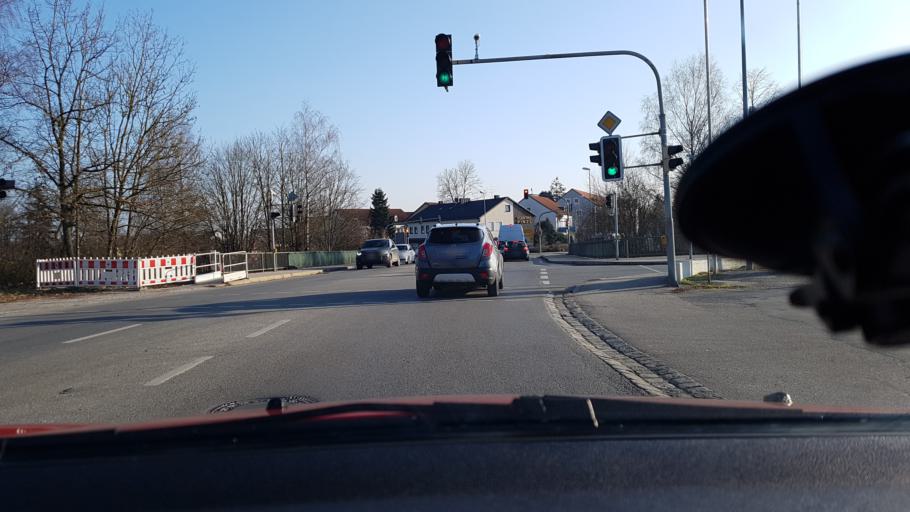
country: DE
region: Bavaria
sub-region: Lower Bavaria
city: Simbach am Inn
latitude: 48.2713
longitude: 13.0199
